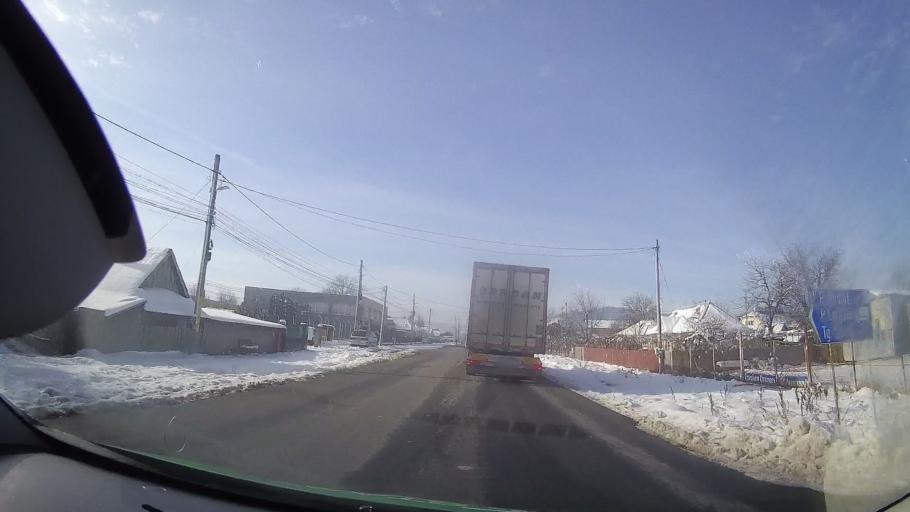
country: RO
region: Neamt
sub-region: Oras Targu Neamt
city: Targu Neamt
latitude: 47.2087
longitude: 26.3894
